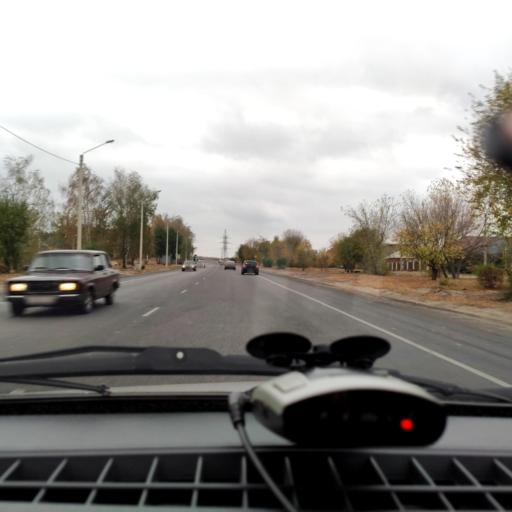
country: RU
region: Voronezj
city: Pridonskoy
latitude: 51.7022
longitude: 39.0774
